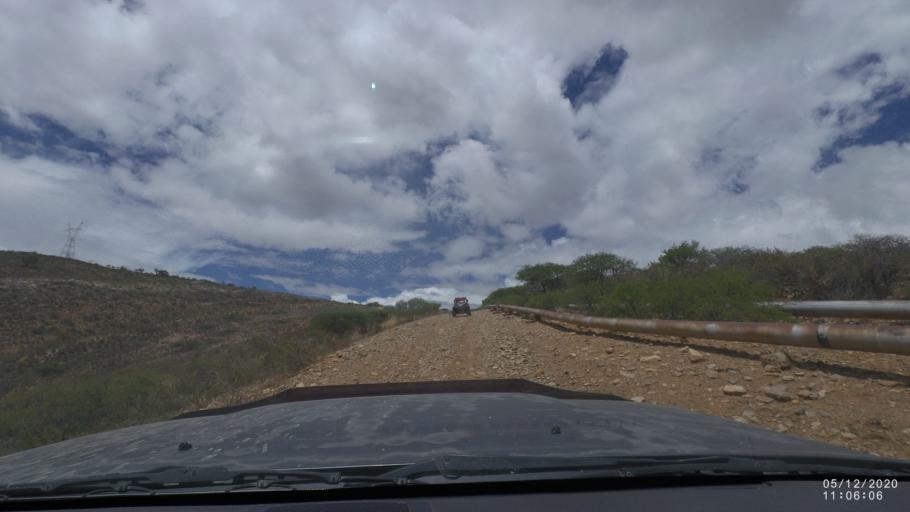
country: BO
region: Cochabamba
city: Sipe Sipe
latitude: -17.5500
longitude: -66.3055
